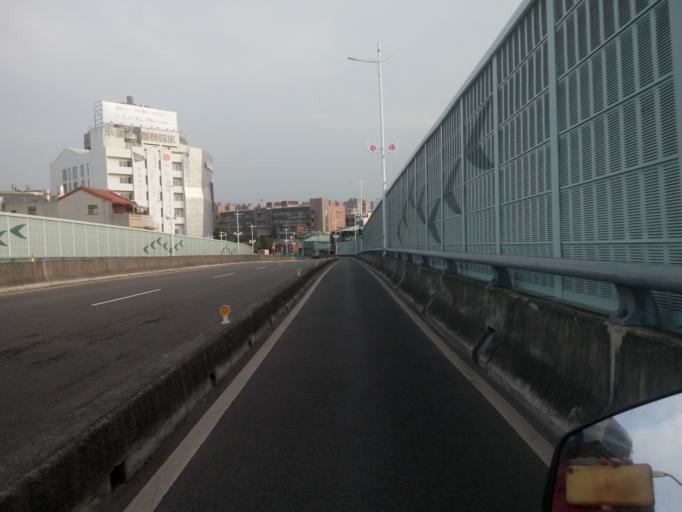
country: TW
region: Taiwan
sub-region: Chiayi
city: Jiayi Shi
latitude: 23.4736
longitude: 120.4362
